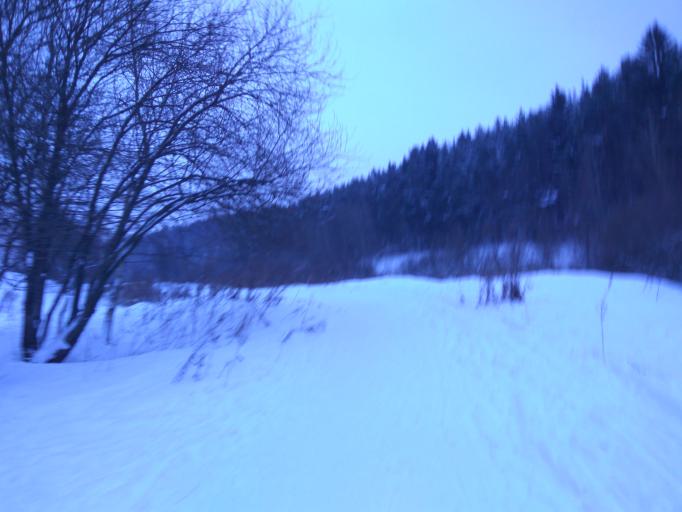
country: RU
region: Moscow
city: Orekhovo-Borisovo Severnoye
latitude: 55.5998
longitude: 37.7023
